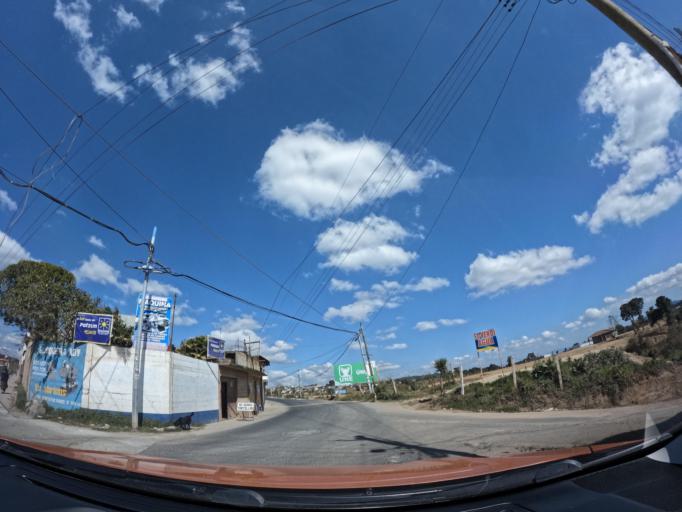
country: GT
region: Chimaltenango
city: Patzun
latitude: 14.6664
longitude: -91.0138
